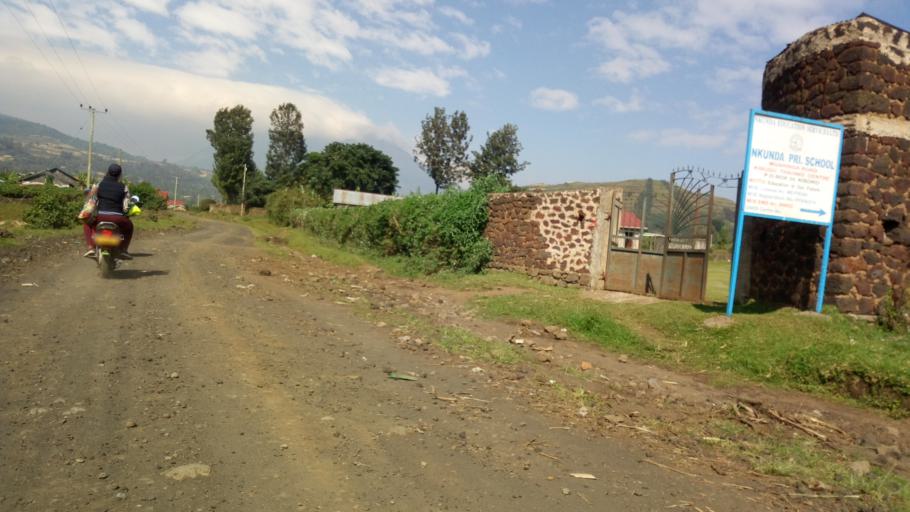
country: UG
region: Western Region
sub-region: Kisoro District
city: Kisoro
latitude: -1.3287
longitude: 29.6413
